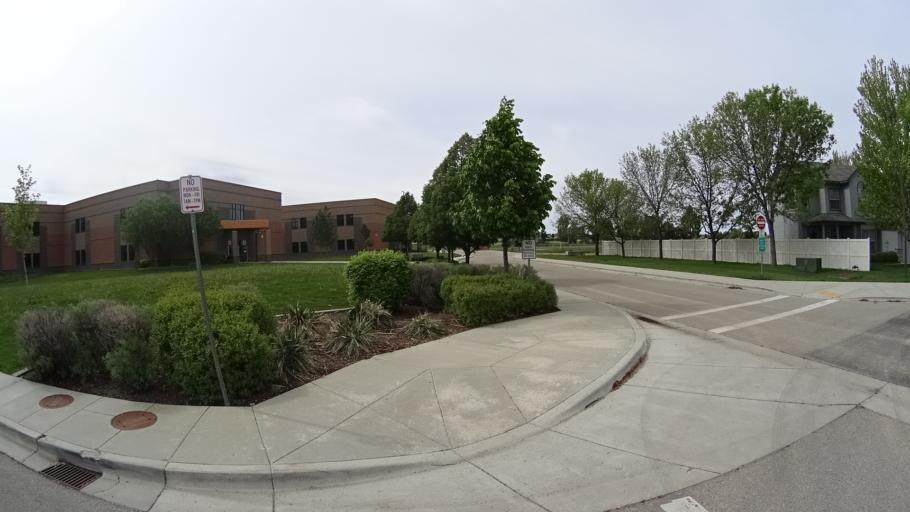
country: US
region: Idaho
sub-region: Ada County
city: Garden City
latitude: 43.5718
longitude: -116.2865
